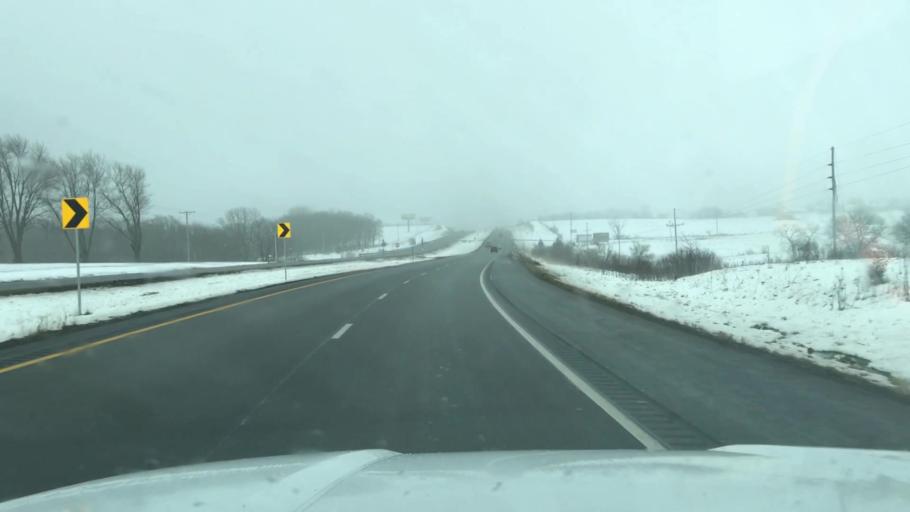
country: US
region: Missouri
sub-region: Clinton County
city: Cameron
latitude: 39.7539
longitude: -94.2674
